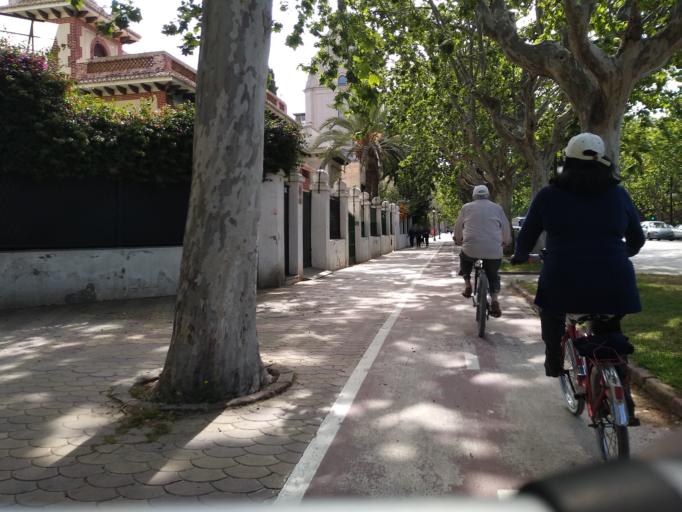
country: ES
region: Valencia
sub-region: Provincia de Valencia
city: Valencia
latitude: 39.4797
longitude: -0.3658
